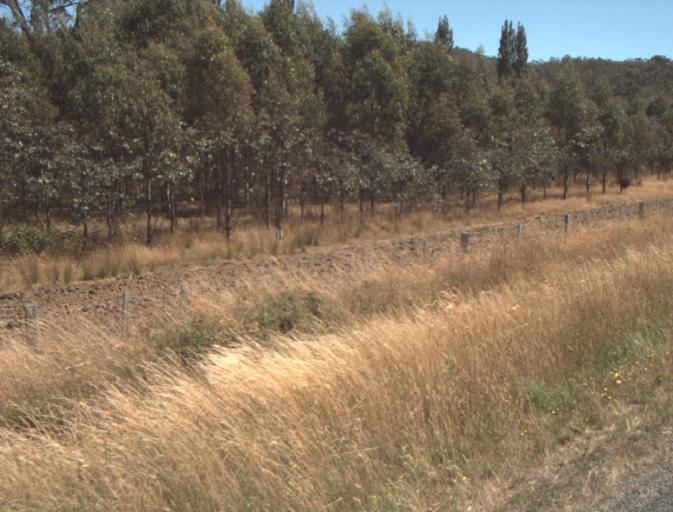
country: AU
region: Tasmania
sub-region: Launceston
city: Newstead
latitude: -41.3809
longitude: 147.3116
